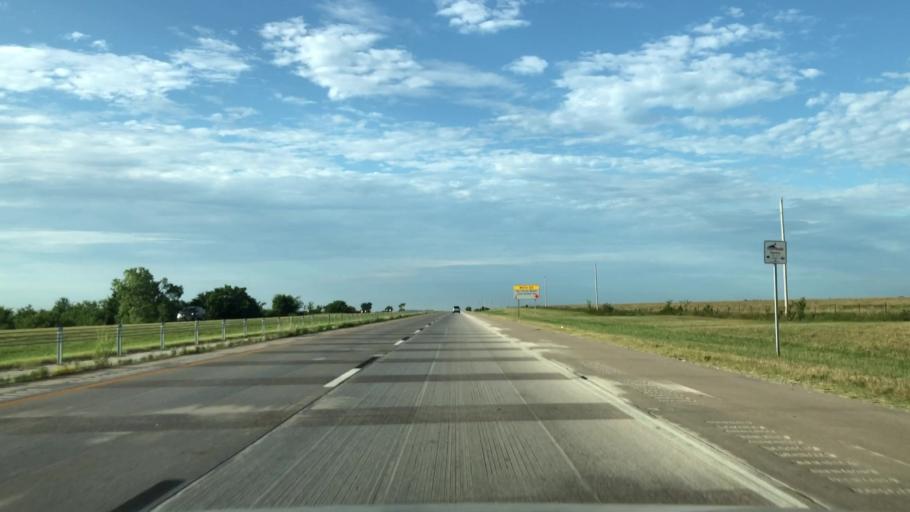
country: US
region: Oklahoma
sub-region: Osage County
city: Skiatook
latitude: 36.4231
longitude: -95.9207
